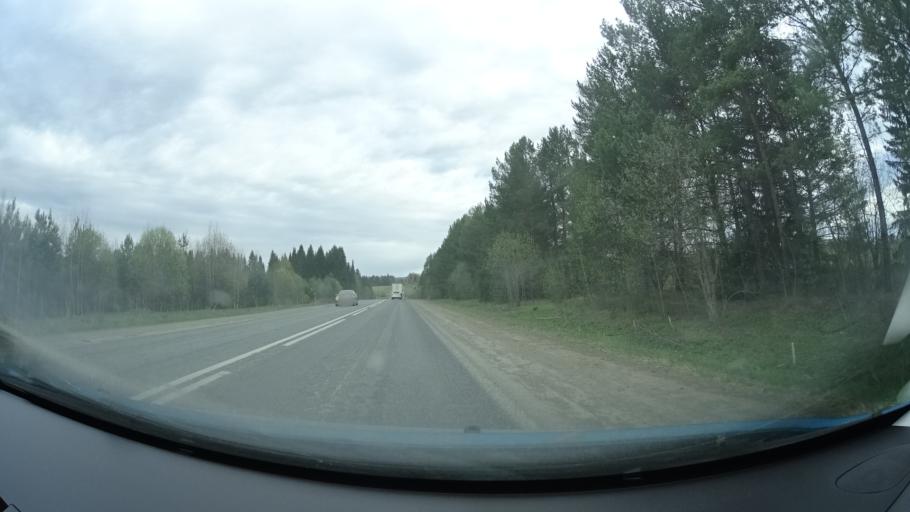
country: RU
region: Perm
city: Yugo-Kamskiy
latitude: 57.6759
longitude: 55.5798
